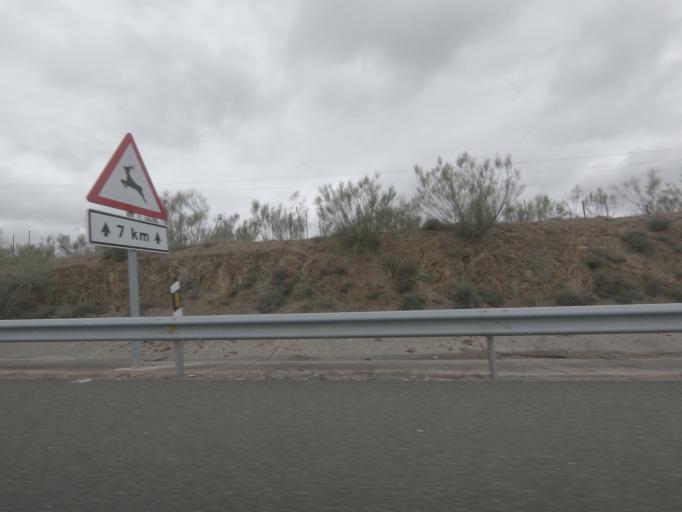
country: ES
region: Extremadura
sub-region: Provincia de Caceres
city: Galisteo
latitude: 39.9291
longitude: -6.2262
